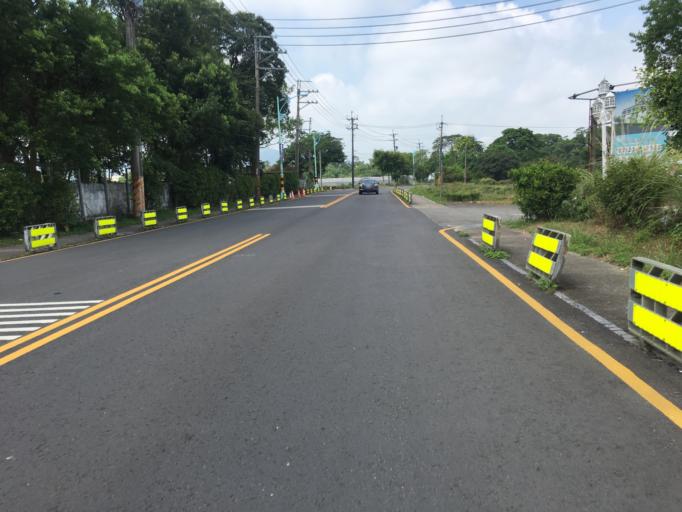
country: TW
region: Taiwan
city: Daxi
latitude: 24.8471
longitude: 121.2436
